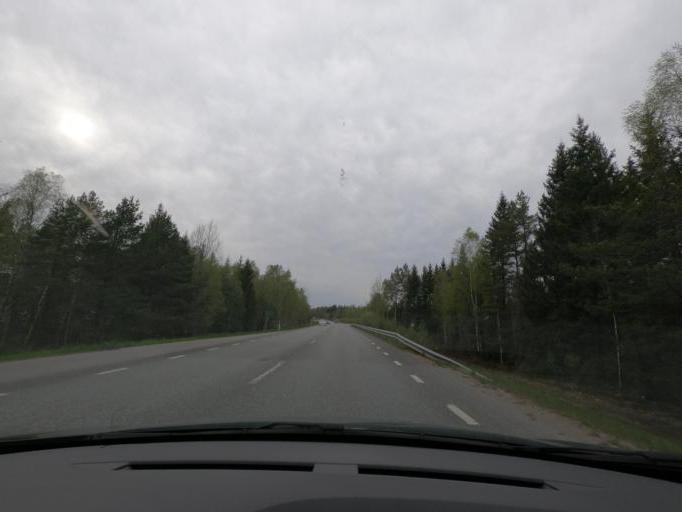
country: SE
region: Vaestra Goetaland
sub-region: Tranemo Kommun
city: Tranemo
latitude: 57.4938
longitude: 13.3598
